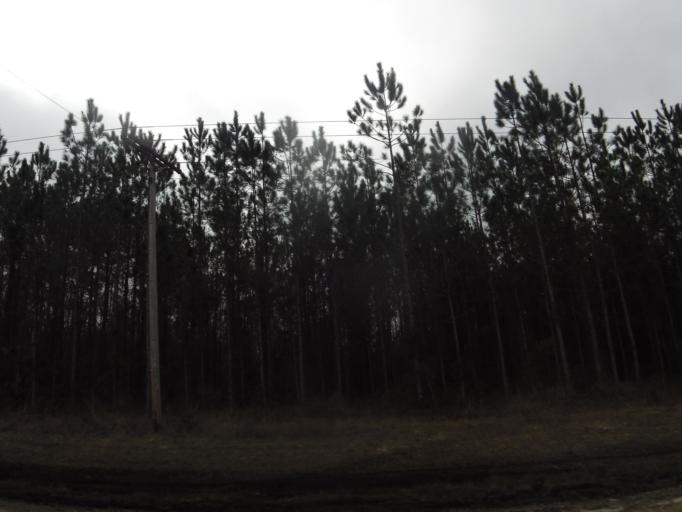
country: US
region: Florida
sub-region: Gilchrist County
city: Trenton
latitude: 29.7915
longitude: -82.7987
